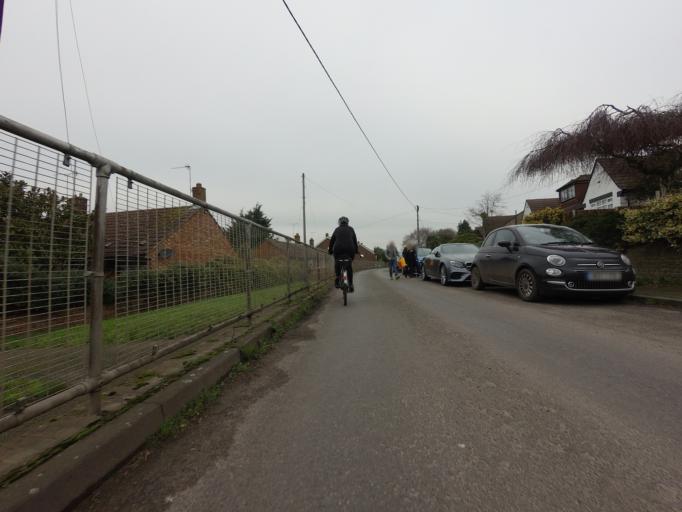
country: GB
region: England
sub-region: Kent
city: Eynsford
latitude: 51.3933
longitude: 0.2459
